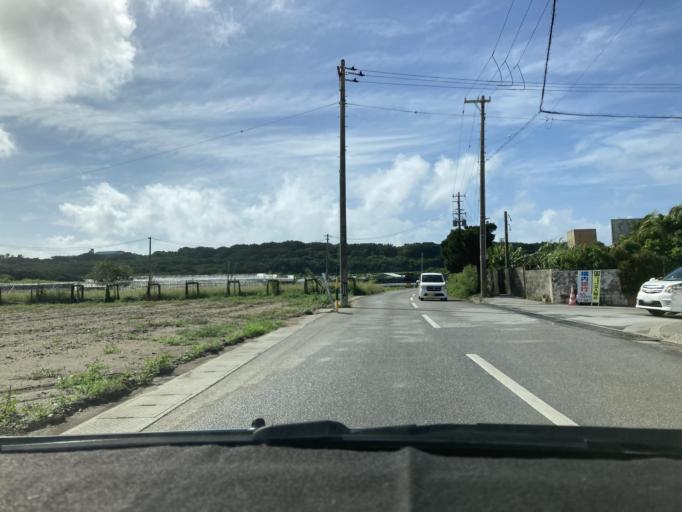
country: JP
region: Okinawa
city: Itoman
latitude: 26.1004
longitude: 127.6616
